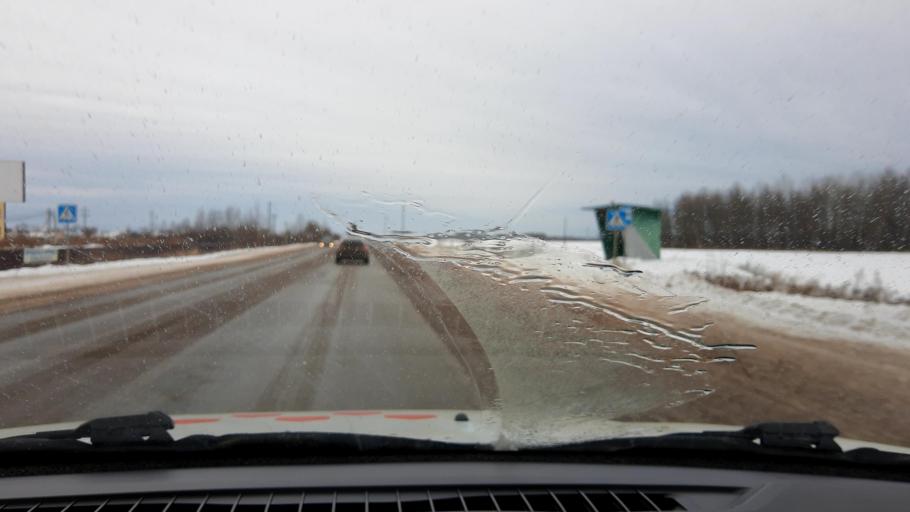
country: RU
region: Nizjnij Novgorod
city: Gorodets
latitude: 56.6623
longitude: 43.4972
